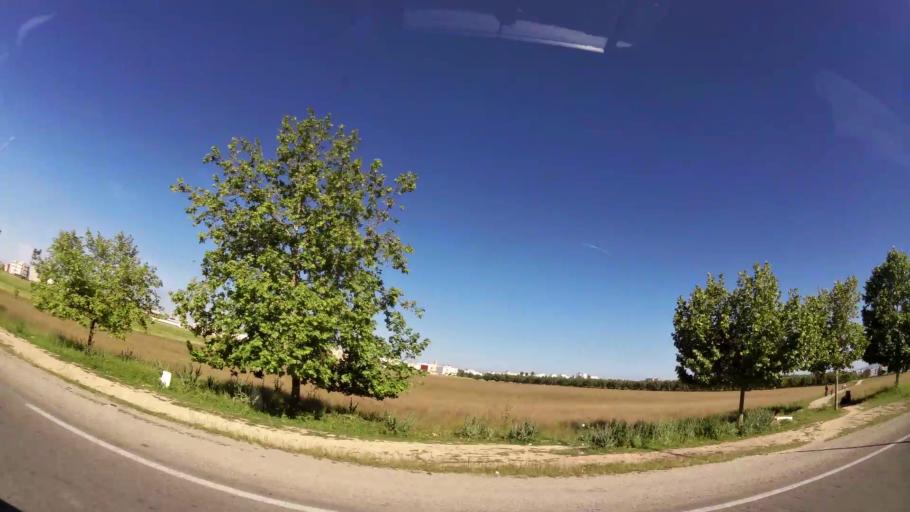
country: MA
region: Fes-Boulemane
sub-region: Fes
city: Fes
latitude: 34.0004
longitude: -5.0239
